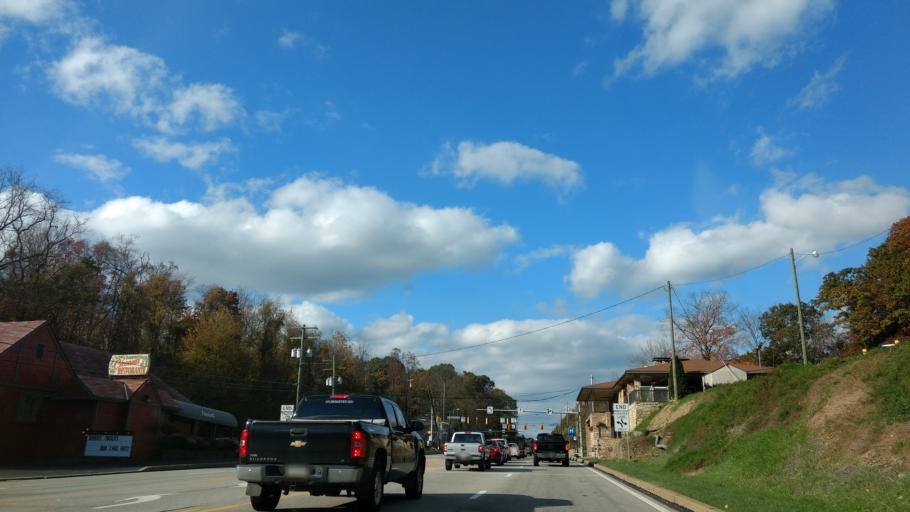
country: US
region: Pennsylvania
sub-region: Allegheny County
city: Jefferson Hills
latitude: 40.3120
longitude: -79.9381
